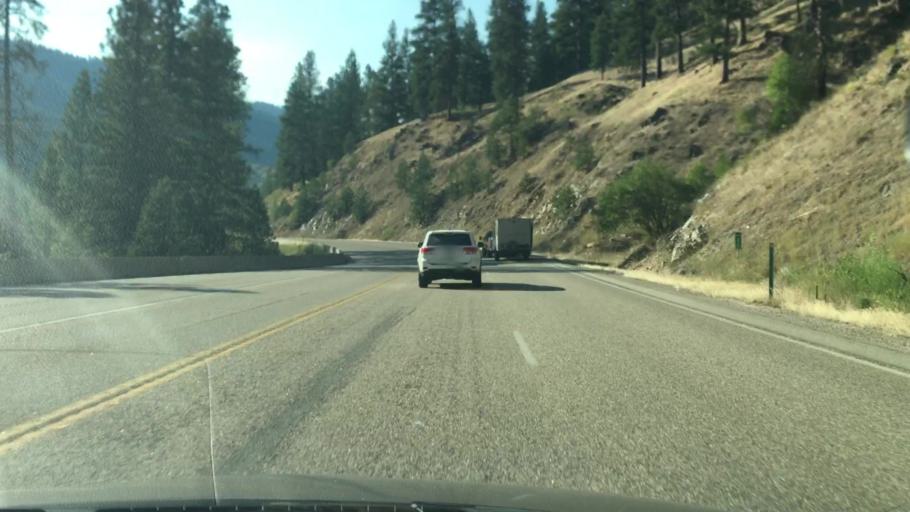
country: US
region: Idaho
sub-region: Boise County
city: Idaho City
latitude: 44.1075
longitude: -116.0956
